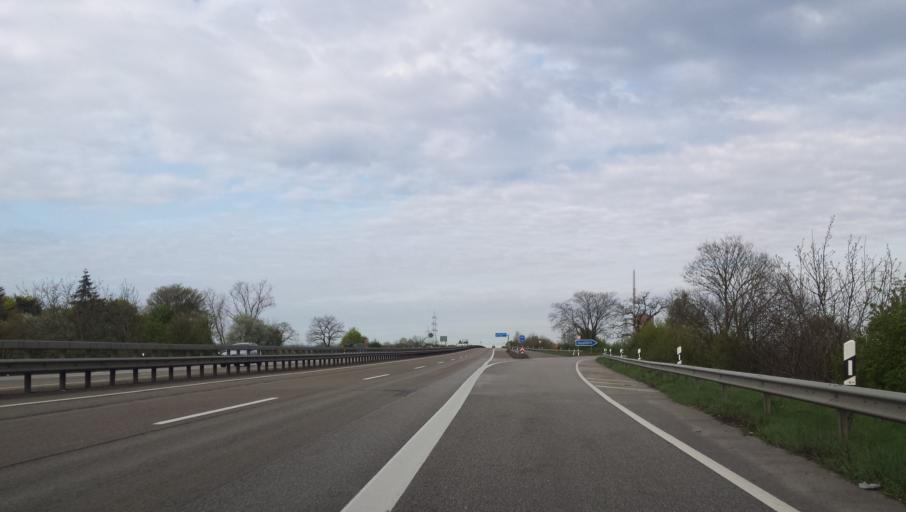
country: DE
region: Rheinland-Pfalz
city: Frankenthal
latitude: 49.5549
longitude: 8.3588
